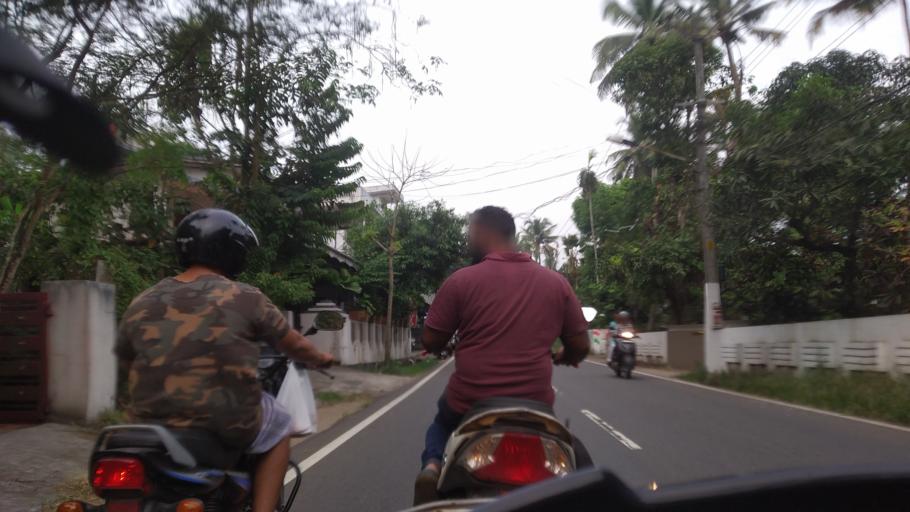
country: IN
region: Kerala
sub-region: Ernakulam
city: Elur
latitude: 10.1502
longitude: 76.2637
